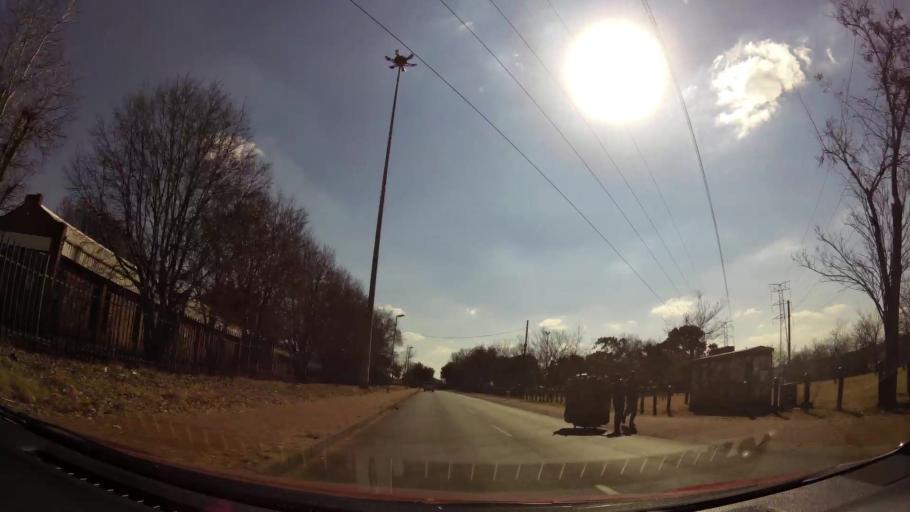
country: ZA
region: Gauteng
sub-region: City of Johannesburg Metropolitan Municipality
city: Soweto
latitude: -26.2432
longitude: 27.8878
